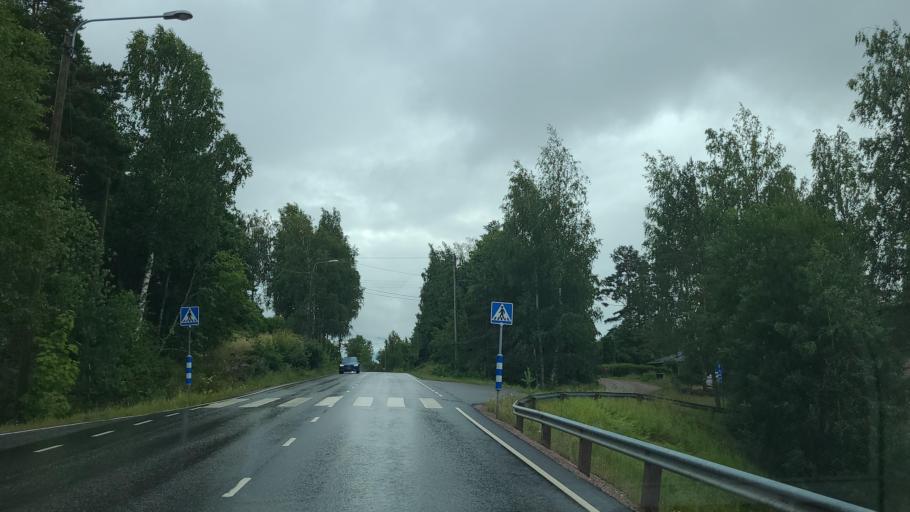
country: FI
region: Varsinais-Suomi
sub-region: Aboland-Turunmaa
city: Kimito
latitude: 60.1717
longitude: 22.7353
